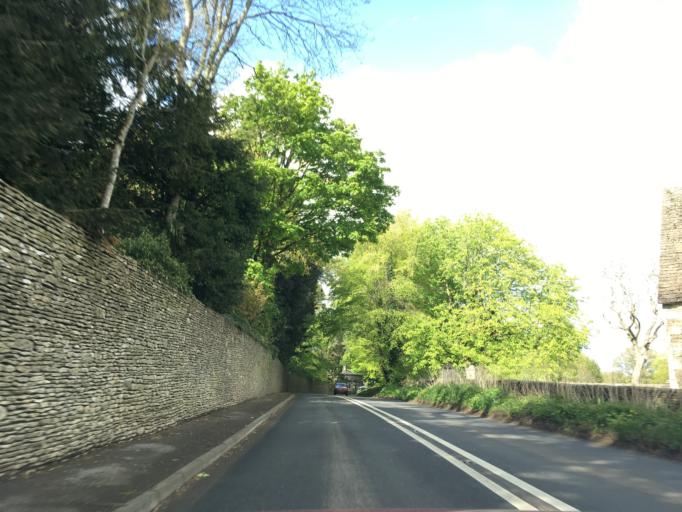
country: GB
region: England
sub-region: Gloucestershire
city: Tetbury
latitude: 51.6217
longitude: -2.1763
